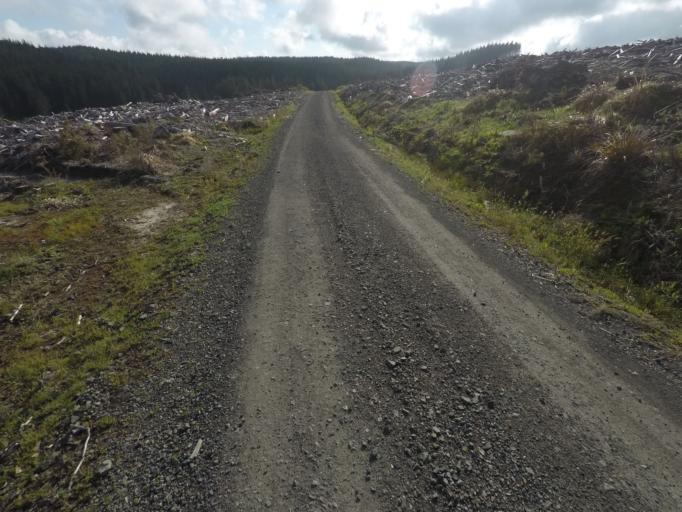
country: NZ
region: Auckland
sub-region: Auckland
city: Parakai
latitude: -36.7134
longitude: 174.5684
